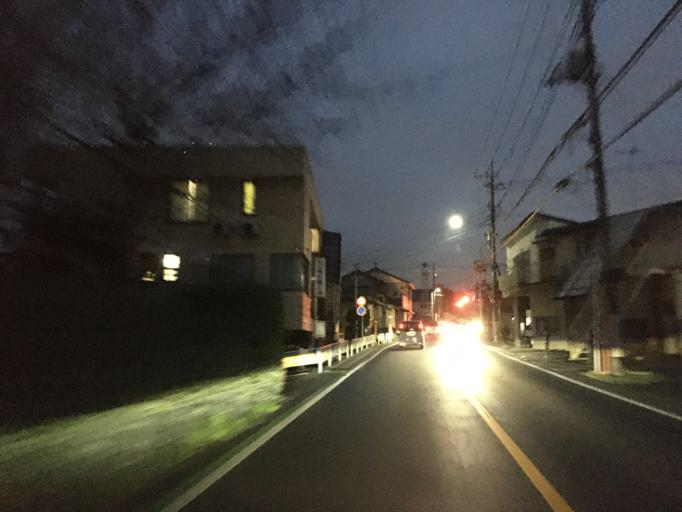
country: JP
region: Saitama
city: Oi
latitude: 35.8070
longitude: 139.5383
